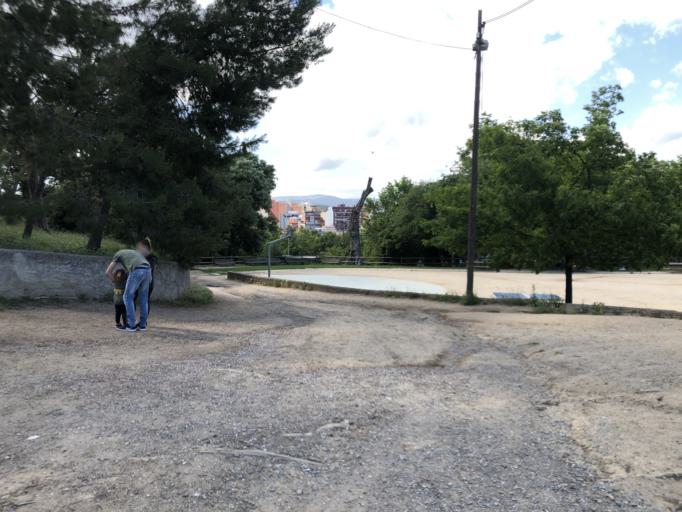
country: ES
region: Catalonia
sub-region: Provincia de Barcelona
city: Rubi
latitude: 41.4927
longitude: 2.0414
